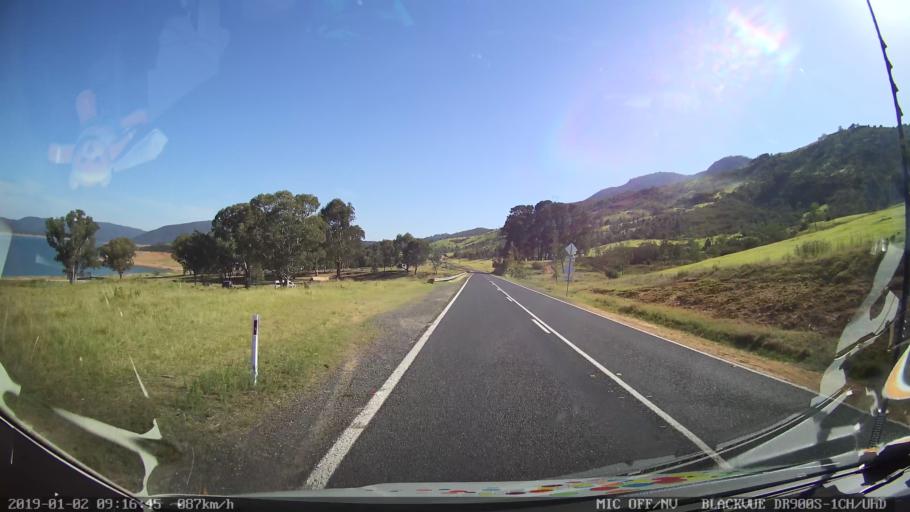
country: AU
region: New South Wales
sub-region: Tumut Shire
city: Tumut
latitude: -35.4496
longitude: 148.2850
